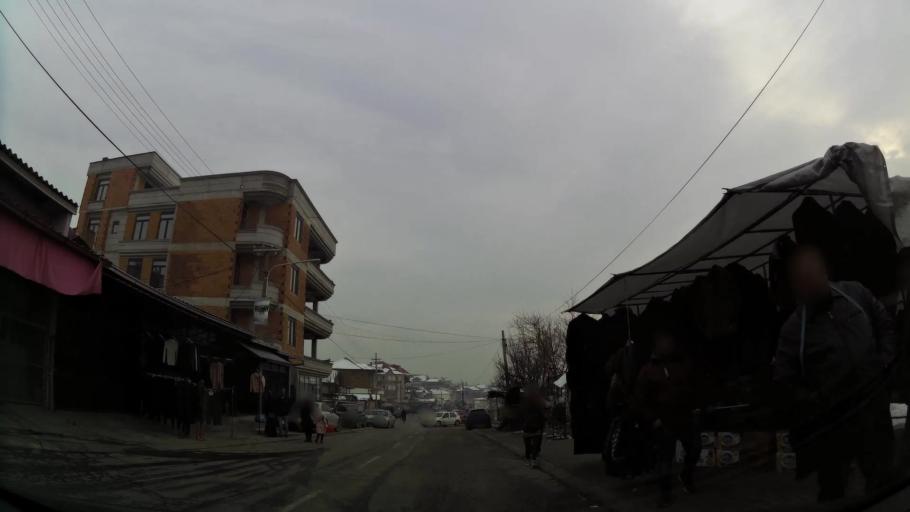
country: MK
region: Suto Orizari
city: Suto Orizare
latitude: 42.0388
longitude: 21.4249
